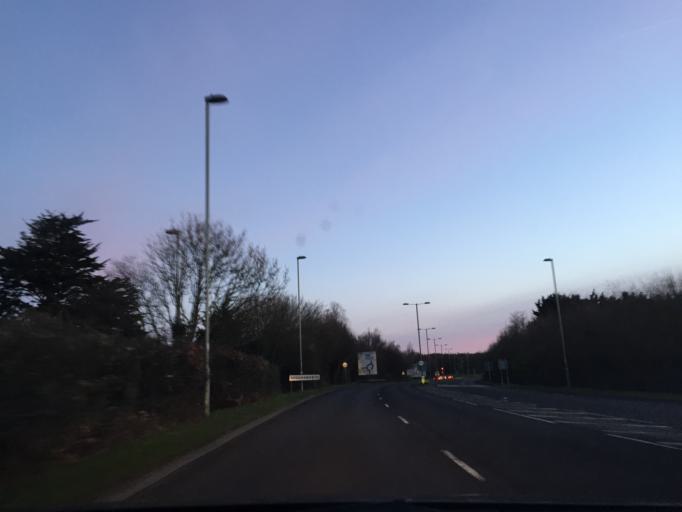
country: GB
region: England
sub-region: Hampshire
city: Botley
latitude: 50.8652
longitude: -1.2555
